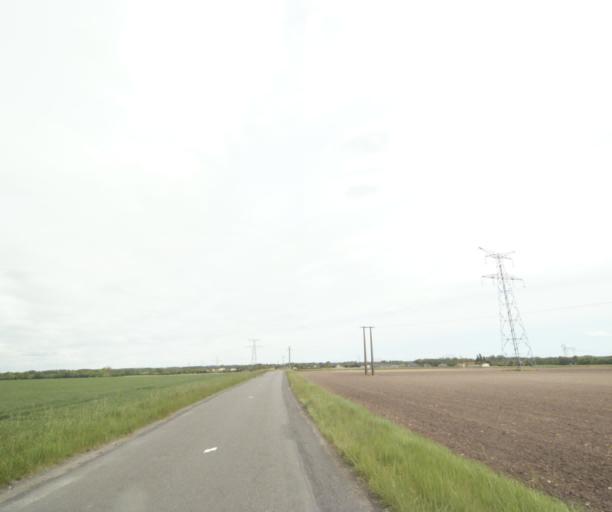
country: FR
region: Poitou-Charentes
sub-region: Departement de la Charente-Maritime
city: Les Gonds
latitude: 45.6888
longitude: -0.6058
